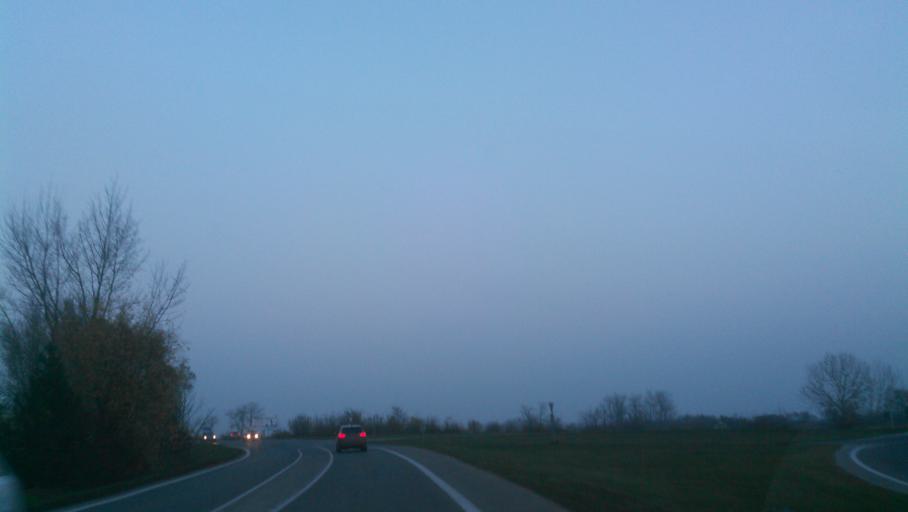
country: SK
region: Bratislavsky
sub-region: Okres Pezinok
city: Pezinok
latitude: 48.2886
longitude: 17.2781
